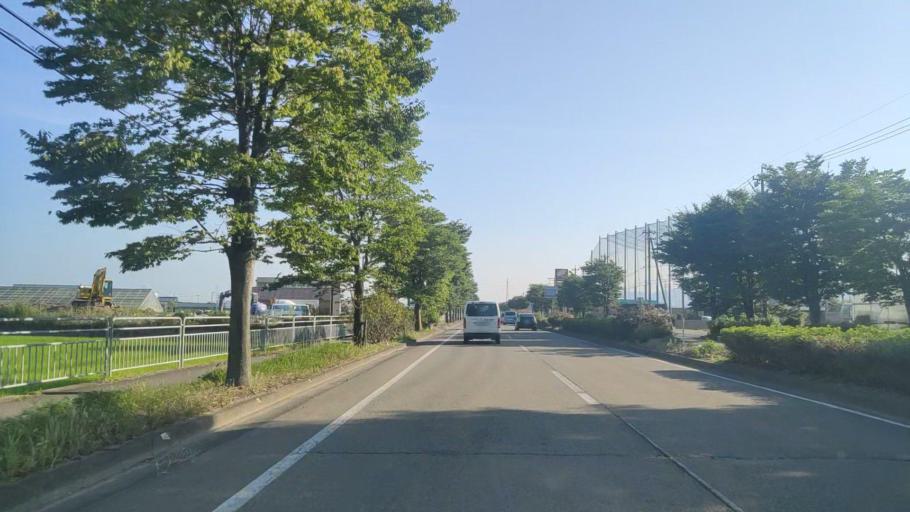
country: JP
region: Fukui
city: Maruoka
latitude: 36.1290
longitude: 136.2608
